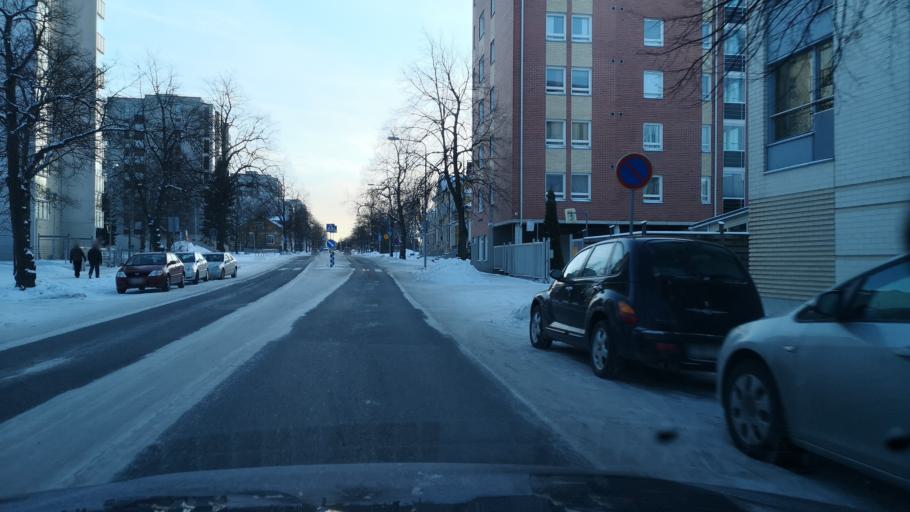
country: FI
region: Satakunta
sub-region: Pori
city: Pori
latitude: 61.4875
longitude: 21.7841
